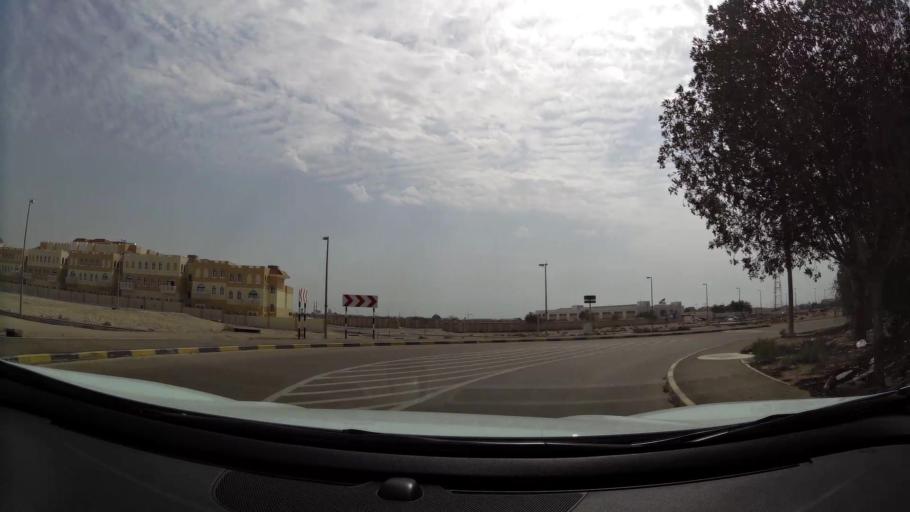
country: AE
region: Abu Dhabi
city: Abu Dhabi
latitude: 24.5528
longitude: 54.6898
